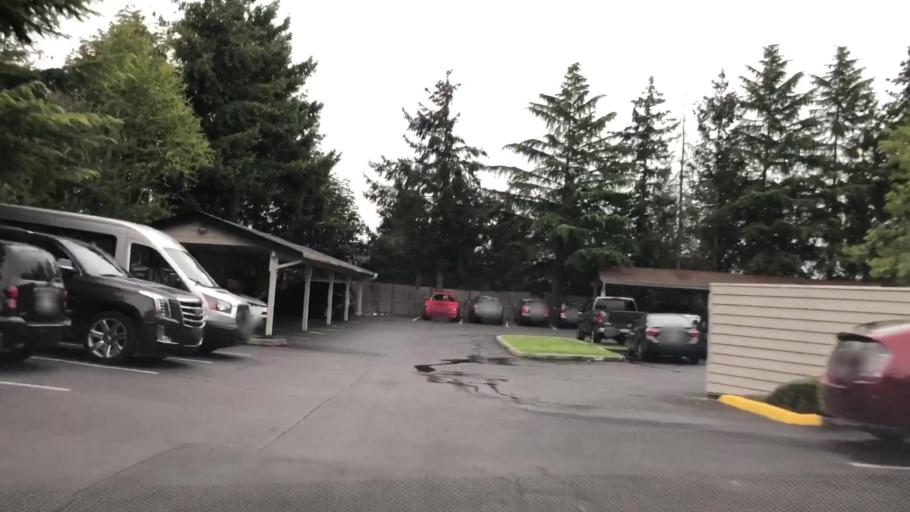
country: US
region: Washington
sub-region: King County
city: Sammamish
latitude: 47.6618
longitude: -122.0904
